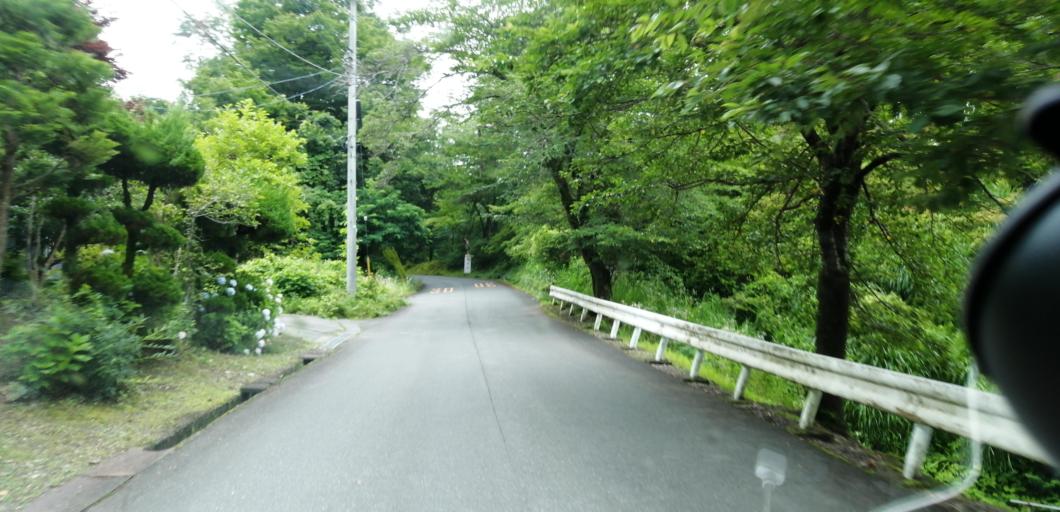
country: JP
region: Saitama
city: Chichibu
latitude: 36.0370
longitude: 139.1119
